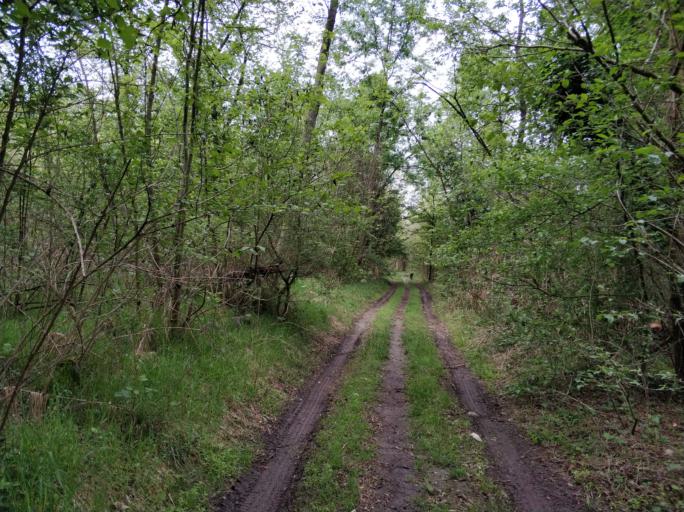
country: IT
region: Piedmont
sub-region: Provincia di Torino
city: Robassomero
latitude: 45.2190
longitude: 7.5693
